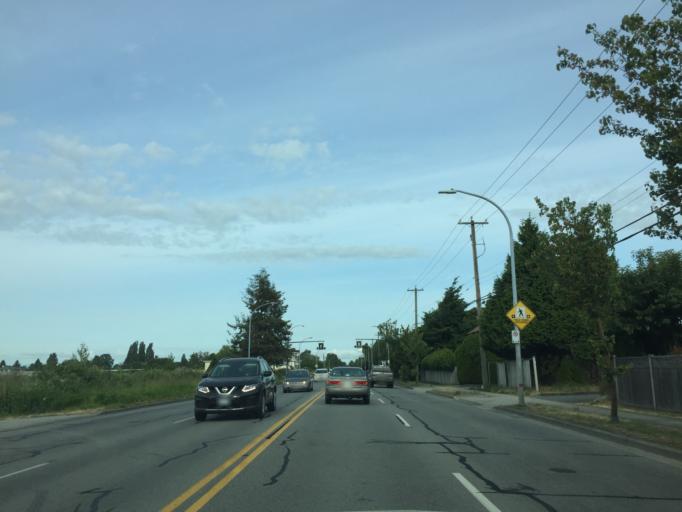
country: CA
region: British Columbia
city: Richmond
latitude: 49.1335
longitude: -123.1500
